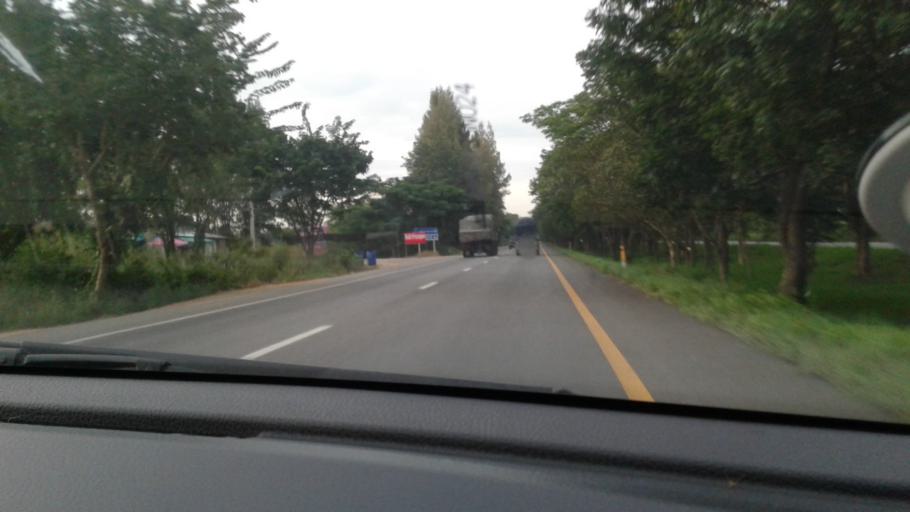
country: TH
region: Prachuap Khiri Khan
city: Pran Buri
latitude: 12.4756
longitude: 99.8940
